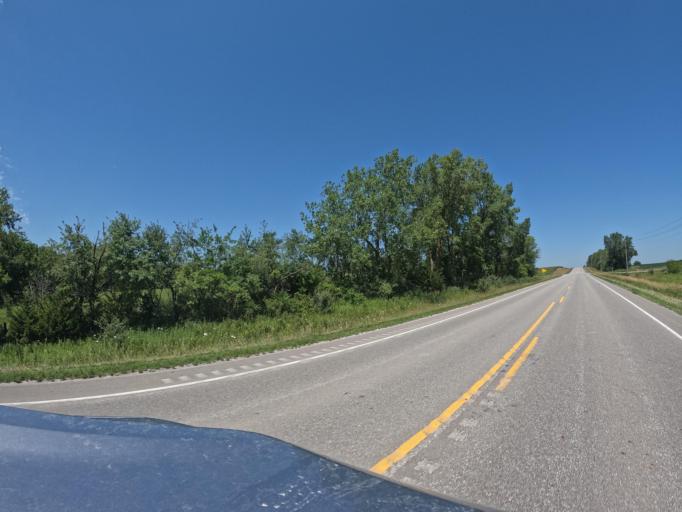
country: US
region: Iowa
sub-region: Keokuk County
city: Sigourney
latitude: 41.4654
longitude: -92.3552
